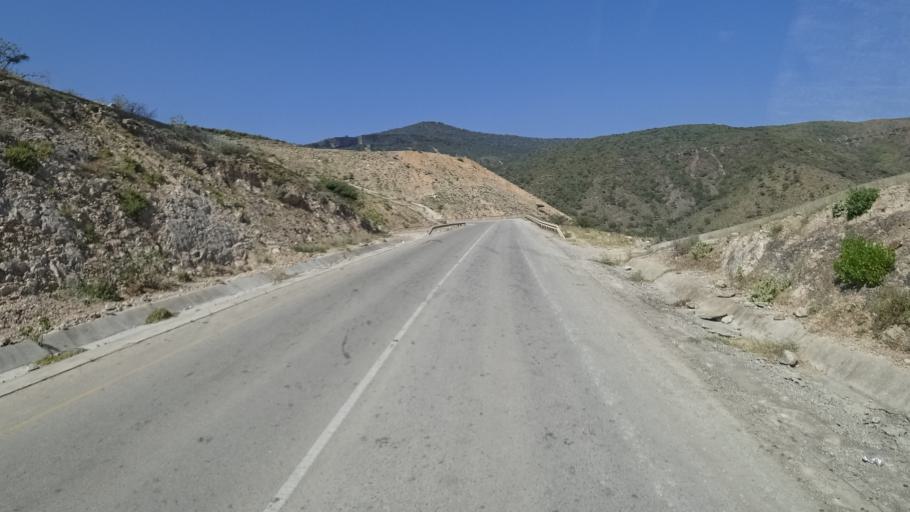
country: OM
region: Zufar
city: Salalah
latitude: 17.0455
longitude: 54.6130
